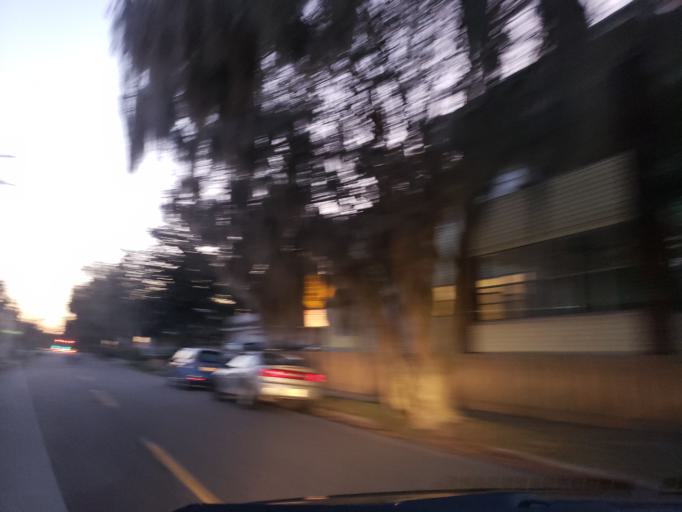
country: US
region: Georgia
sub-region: Chatham County
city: Savannah
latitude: 32.0520
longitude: -81.0882
